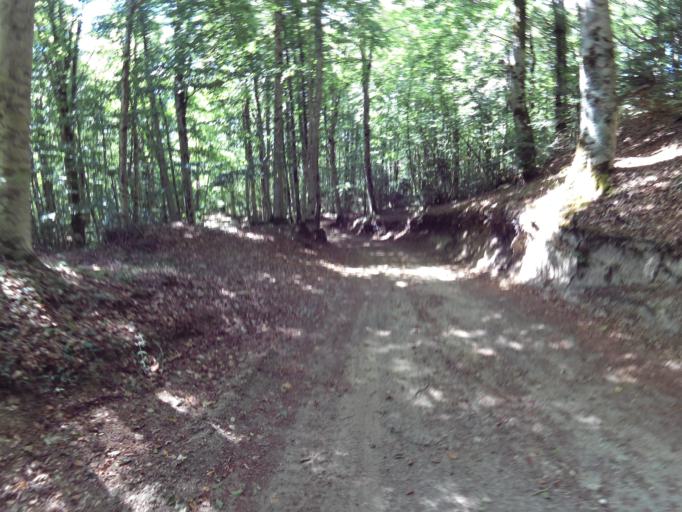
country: IT
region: Calabria
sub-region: Provincia di Vibo-Valentia
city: Mongiana
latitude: 38.5190
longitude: 16.3452
